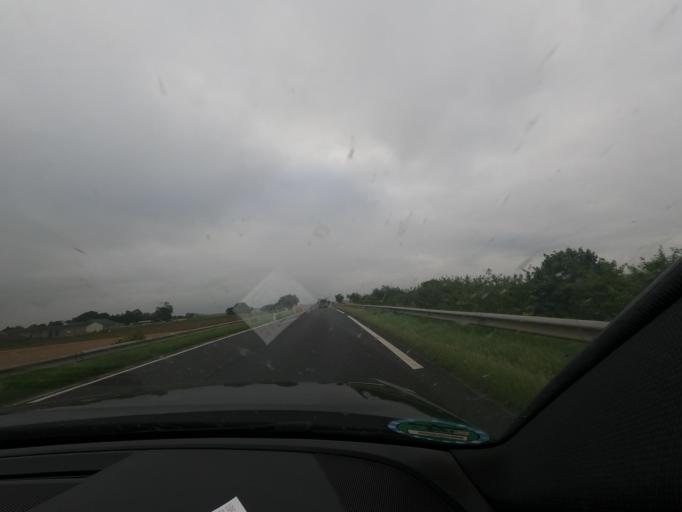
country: FR
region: Picardie
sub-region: Departement de la Somme
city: Rosieres-en-Santerre
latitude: 49.7478
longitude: 2.6653
